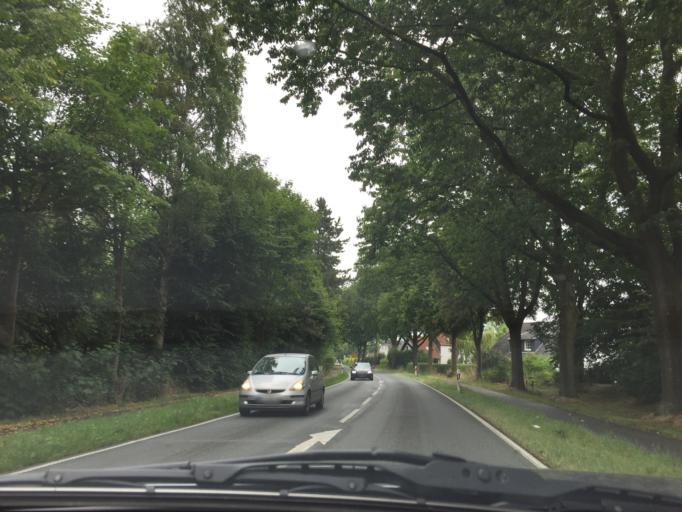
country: DE
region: North Rhine-Westphalia
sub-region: Regierungsbezirk Dusseldorf
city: Kleve
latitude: 51.7582
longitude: 6.1894
